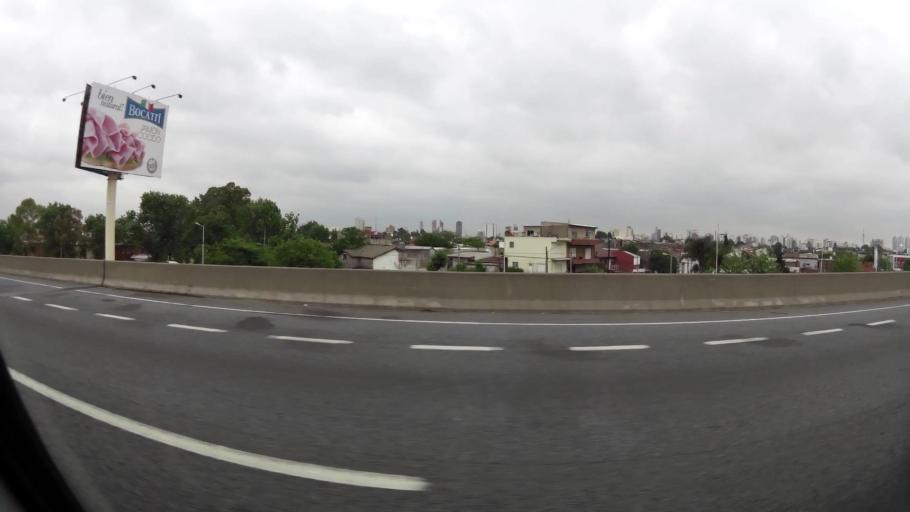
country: AR
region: Buenos Aires
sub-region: Partido de Avellaneda
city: Avellaneda
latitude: -34.6622
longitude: -58.3462
